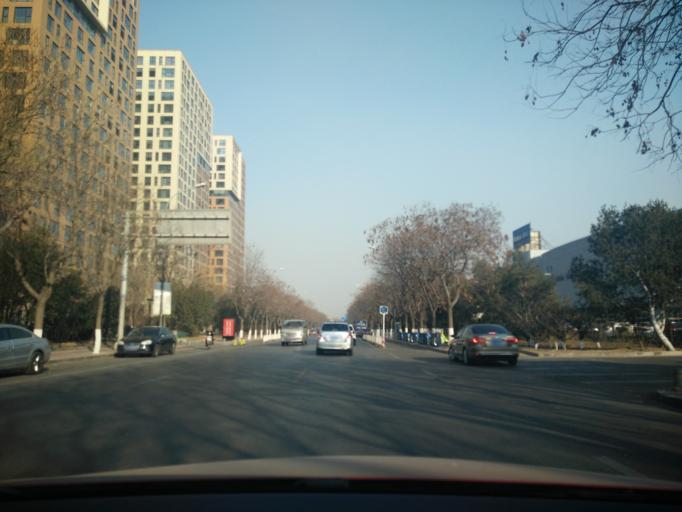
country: CN
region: Beijing
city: Jiugong
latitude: 39.8081
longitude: 116.5015
